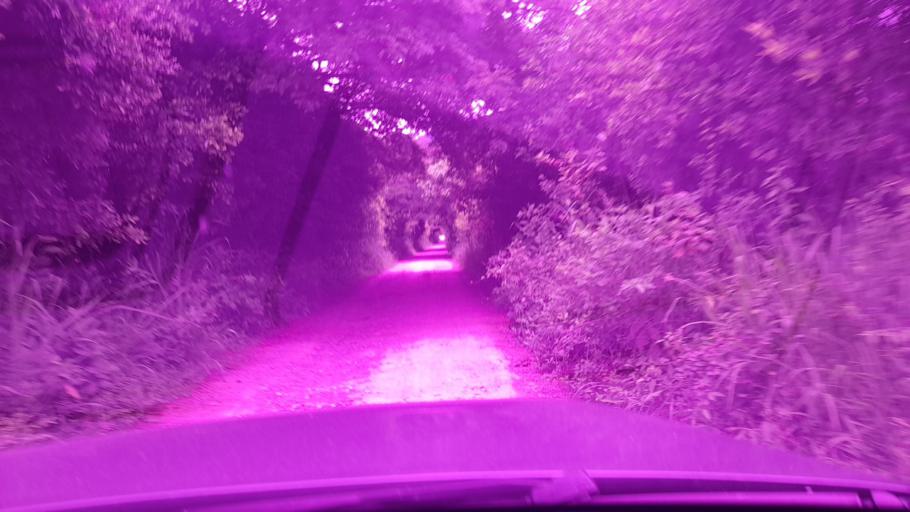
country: CO
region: Valle del Cauca
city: Bugalagrande
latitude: 4.1700
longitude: -76.0764
